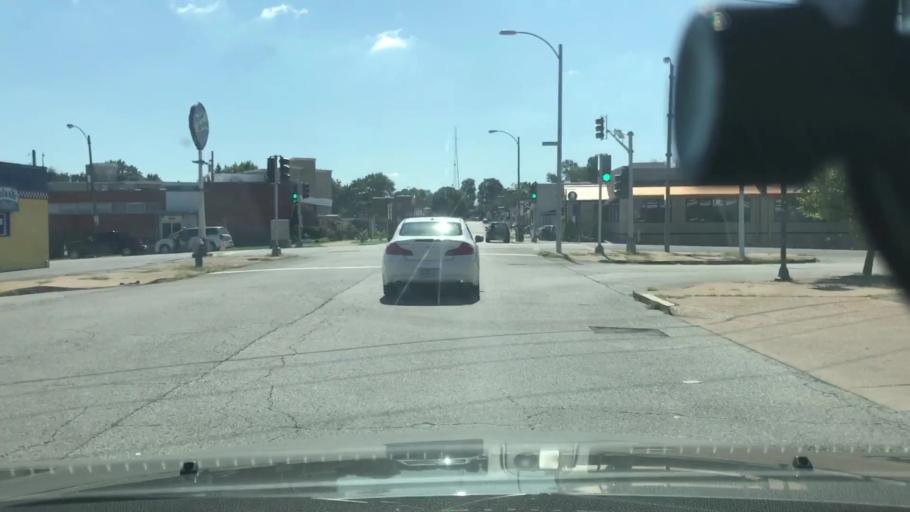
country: US
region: Missouri
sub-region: Saint Louis County
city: Maplewood
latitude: 38.6100
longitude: -90.2899
